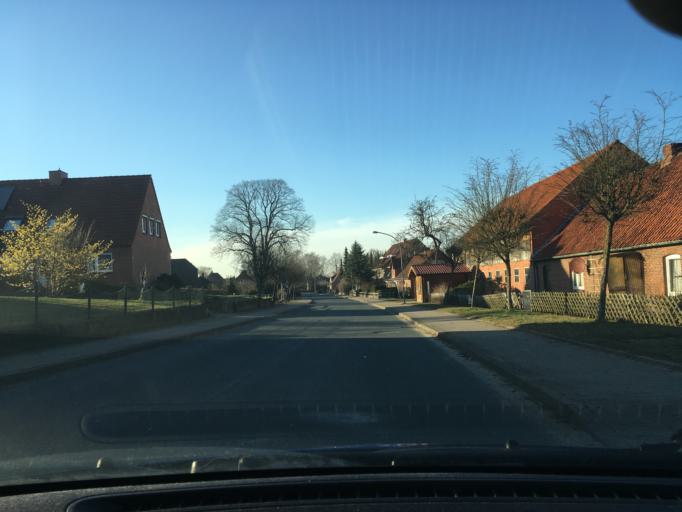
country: DE
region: Schleswig-Holstein
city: Mussen
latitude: 53.4944
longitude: 10.5624
